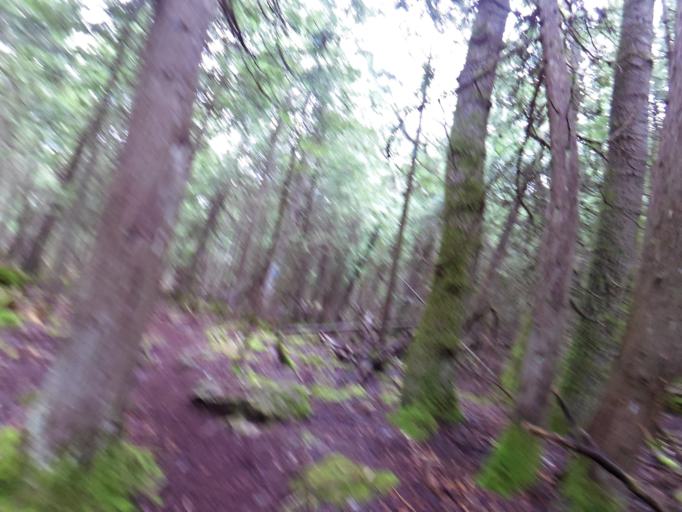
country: CA
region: Ontario
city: Tobermory
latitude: 45.2606
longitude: -81.6444
